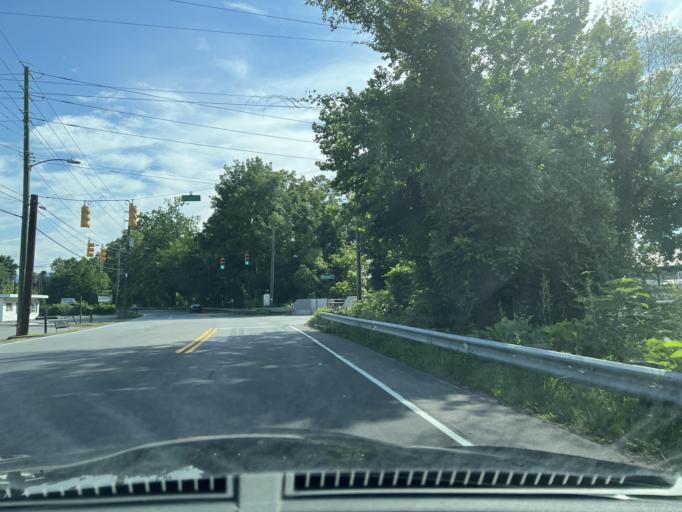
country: US
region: North Carolina
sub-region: Buncombe County
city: Asheville
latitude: 35.5739
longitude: -82.5273
